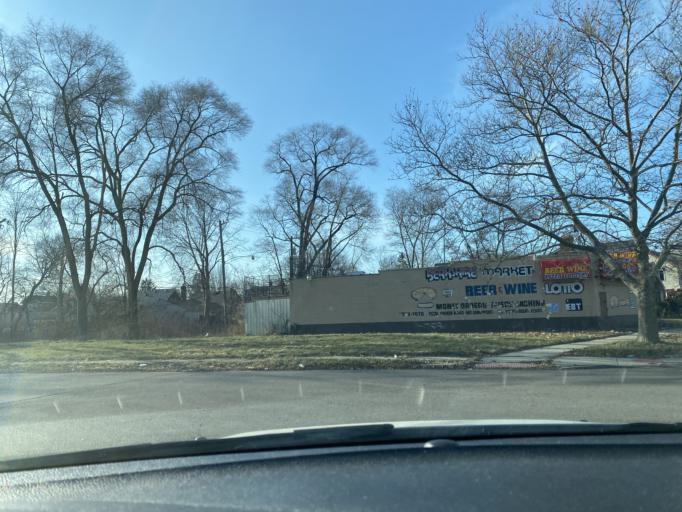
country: US
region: Michigan
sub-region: Wayne County
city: Harper Woods
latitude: 42.4105
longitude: -82.9545
